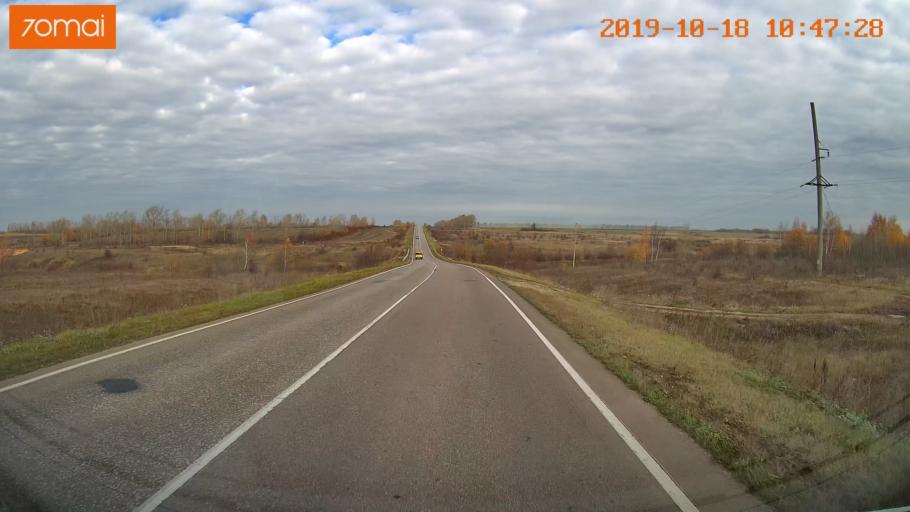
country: RU
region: Tula
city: Yepifan'
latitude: 53.7013
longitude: 38.6976
